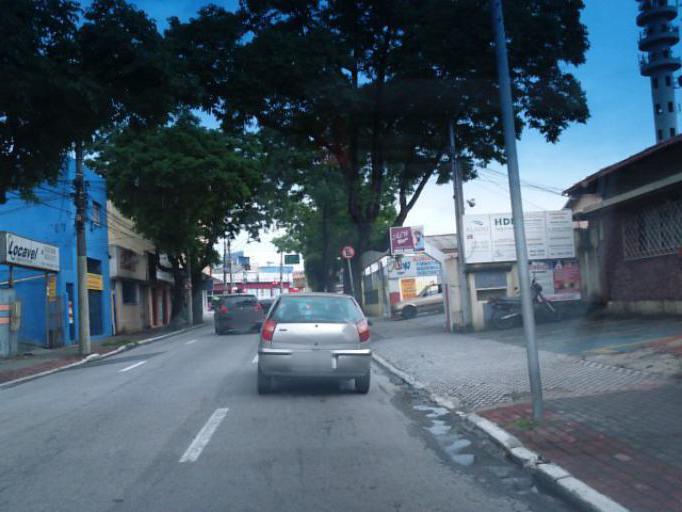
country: BR
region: Sao Paulo
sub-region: Sao Jose Dos Campos
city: Sao Jose dos Campos
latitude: -23.1859
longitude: -45.8817
